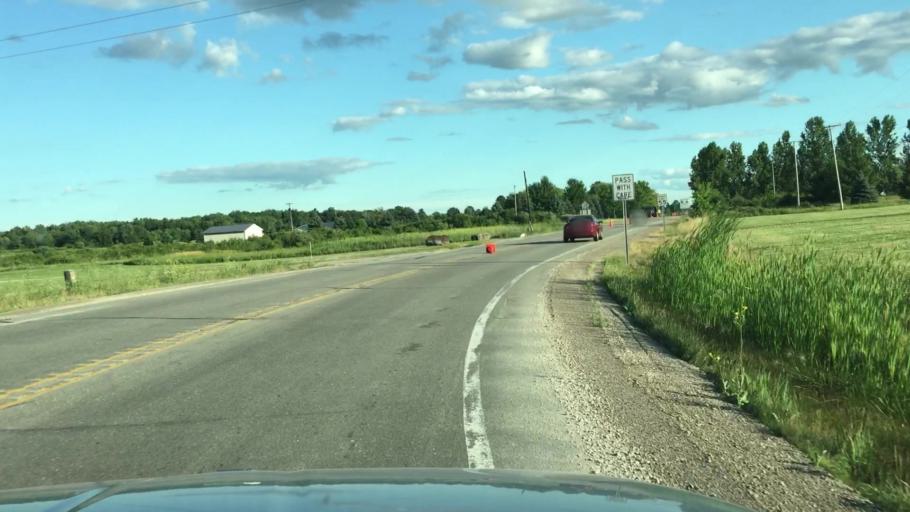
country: US
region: Michigan
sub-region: Saint Clair County
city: Yale
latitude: 43.1012
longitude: -82.7669
